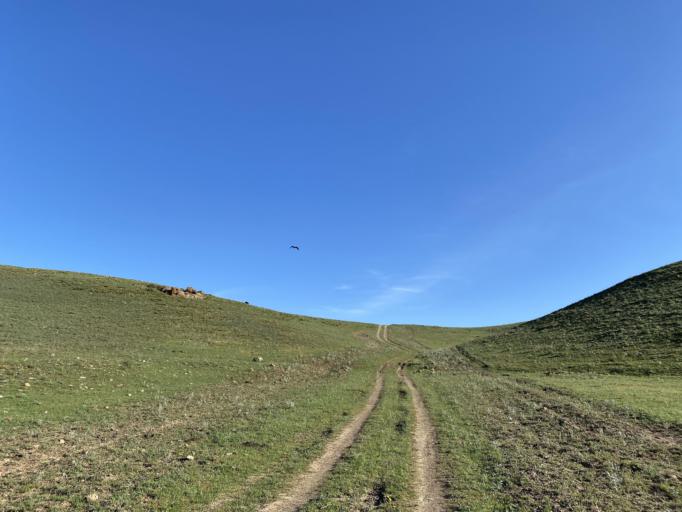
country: KZ
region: Ongtustik Qazaqstan
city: Ashchysay
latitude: 43.7961
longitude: 68.7929
